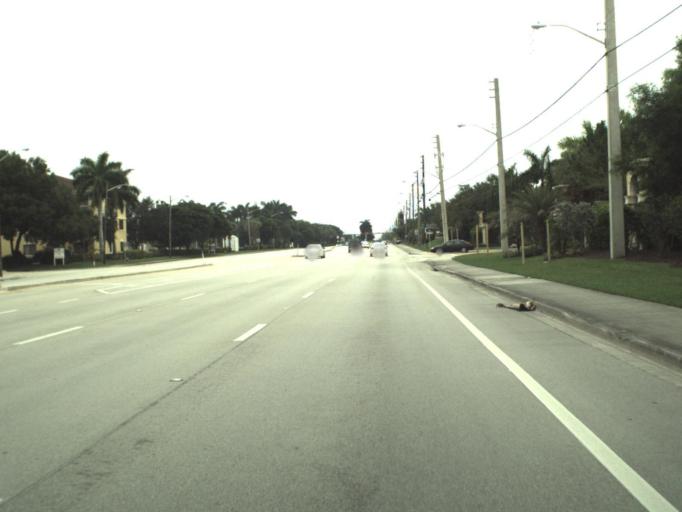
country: US
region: Florida
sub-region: Palm Beach County
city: North Palm Beach
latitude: 26.7878
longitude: -80.1070
